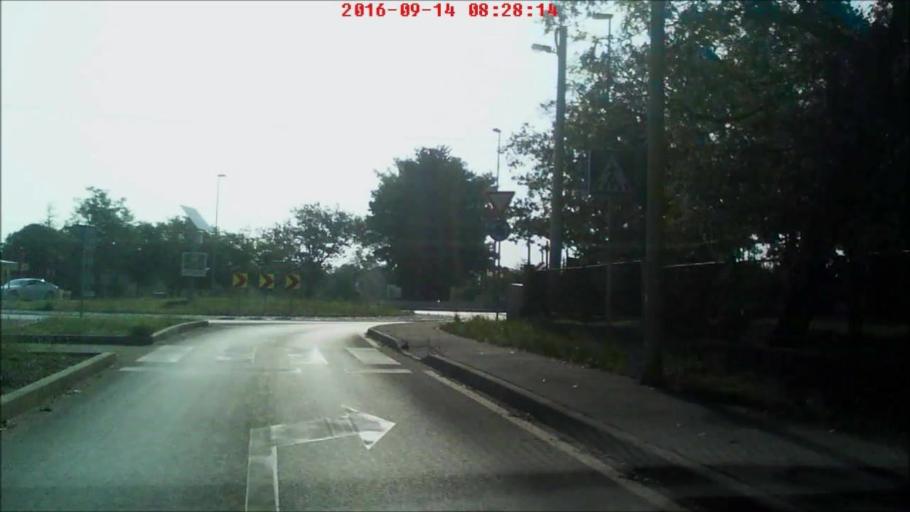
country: HR
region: Zadarska
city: Zadar
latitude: 44.1856
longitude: 15.2746
